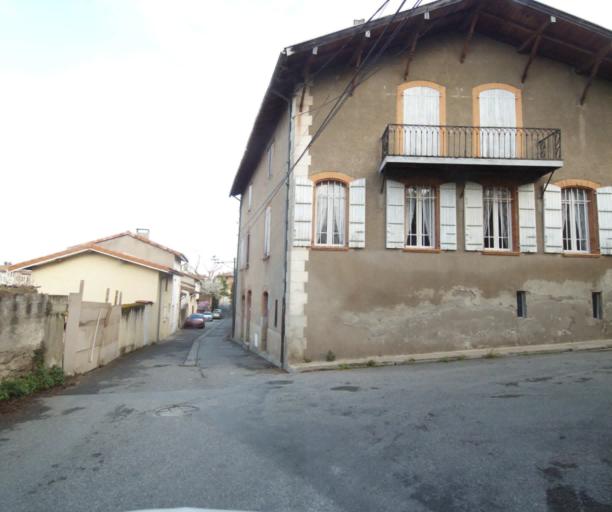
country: FR
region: Midi-Pyrenees
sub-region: Departement de l'Ariege
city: Saverdun
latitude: 43.2316
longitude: 1.5789
